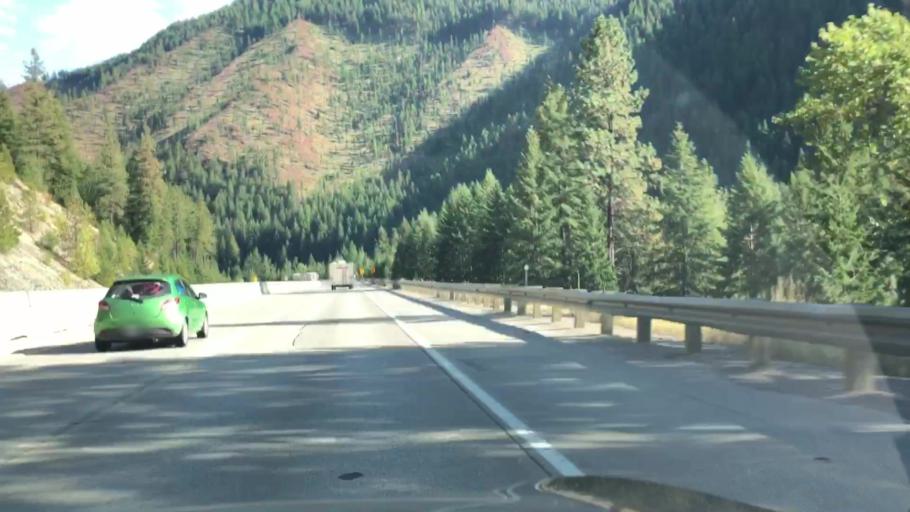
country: US
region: Montana
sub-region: Sanders County
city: Thompson Falls
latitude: 47.3043
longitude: -115.2031
